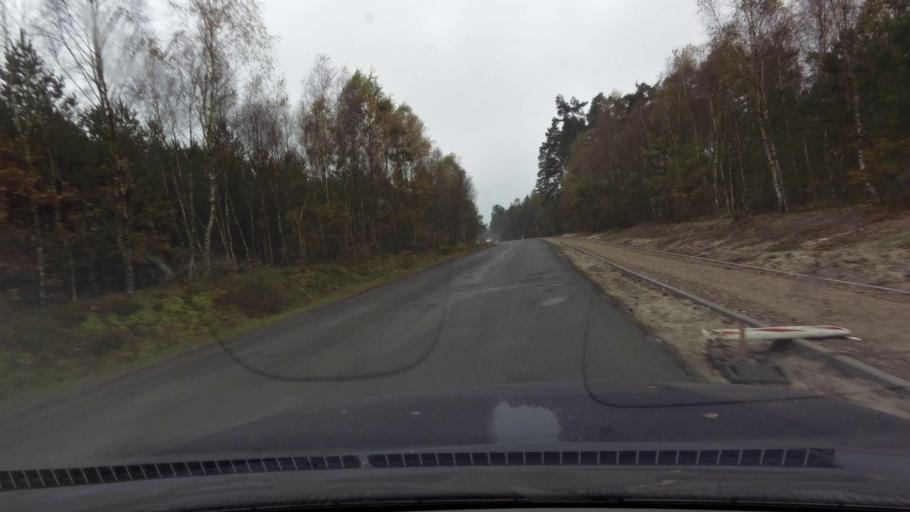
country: PL
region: West Pomeranian Voivodeship
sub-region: Powiat goleniowski
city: Goleniow
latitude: 53.5391
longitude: 14.7663
